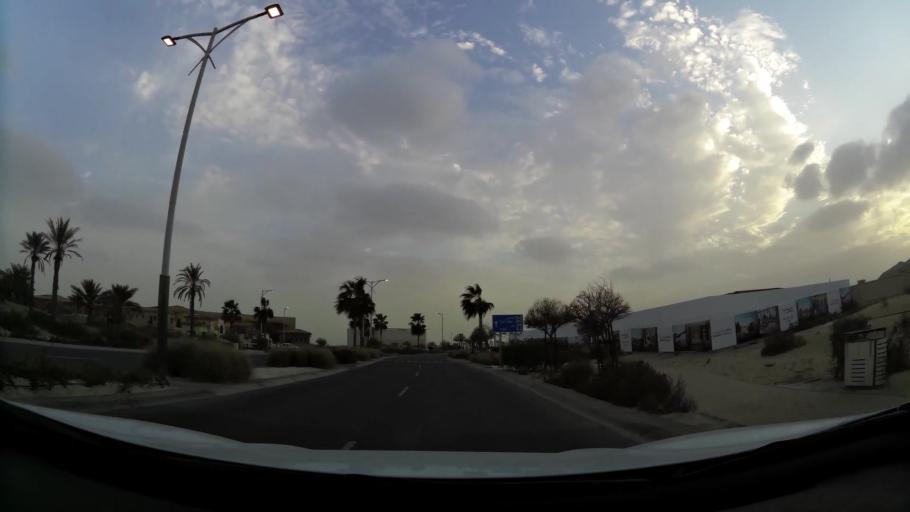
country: AE
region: Abu Dhabi
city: Abu Dhabi
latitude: 24.5355
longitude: 54.4278
